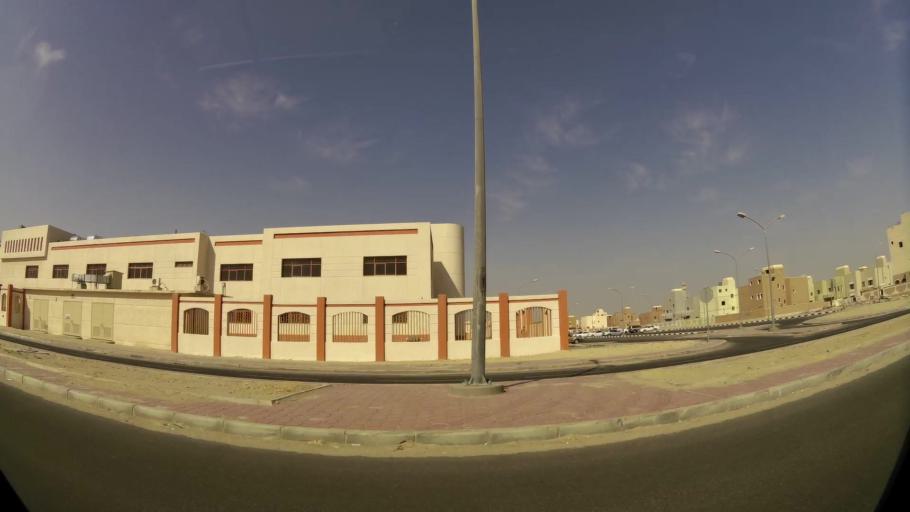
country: KW
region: Al Ahmadi
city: Al Wafrah
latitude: 28.7988
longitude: 48.0735
